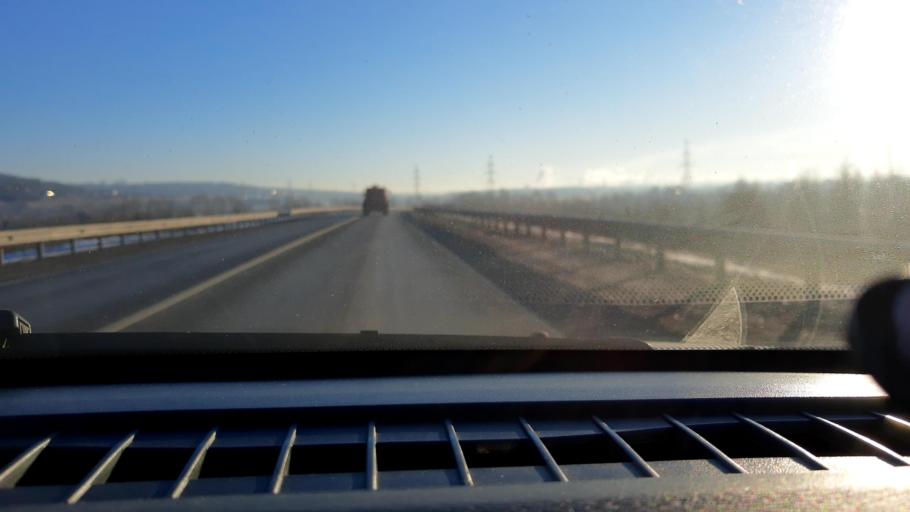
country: RU
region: Nizjnij Novgorod
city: Kstovo
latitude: 56.1528
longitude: 44.1577
